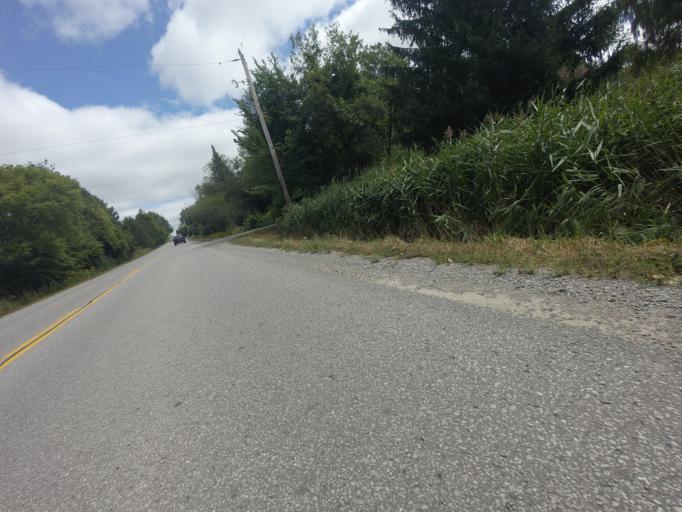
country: CA
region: Ontario
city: Uxbridge
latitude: 44.1239
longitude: -79.1737
